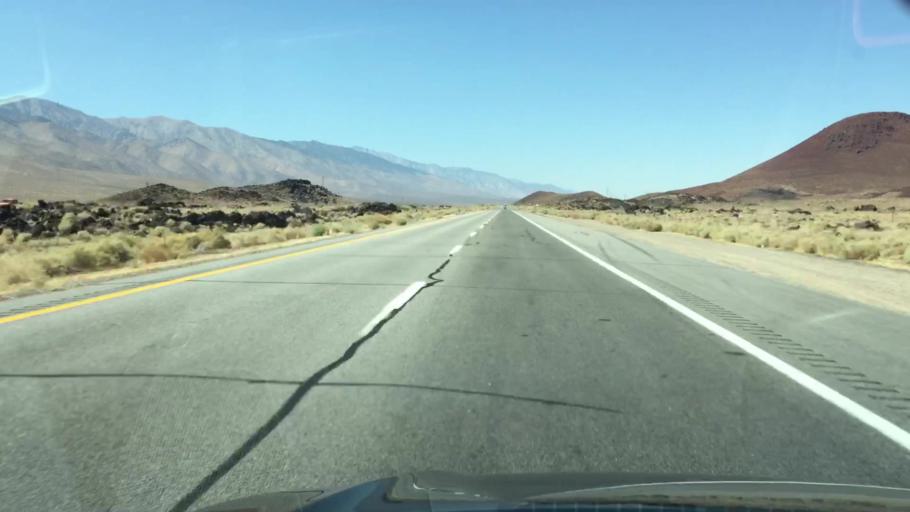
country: US
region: California
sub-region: Kern County
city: Inyokern
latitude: 35.9695
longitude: -117.9197
